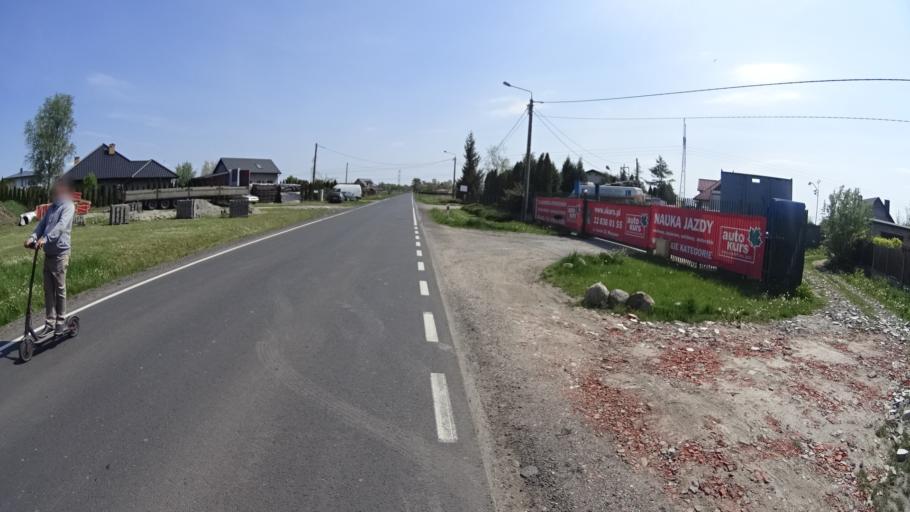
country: PL
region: Masovian Voivodeship
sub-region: Powiat warszawski zachodni
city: Ozarow Mazowiecki
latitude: 52.2393
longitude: 20.7527
